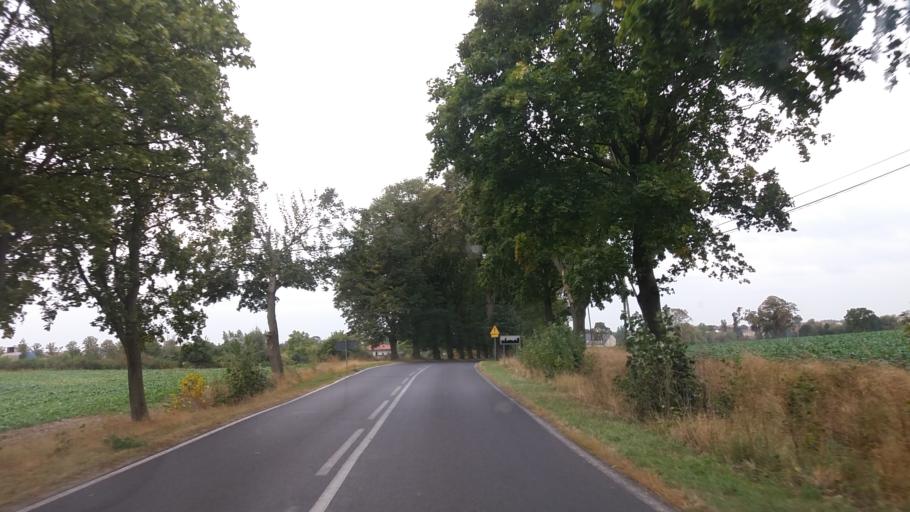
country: PL
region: Lubusz
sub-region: Powiat strzelecko-drezdenecki
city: Strzelce Krajenskie
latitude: 52.8867
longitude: 15.5412
